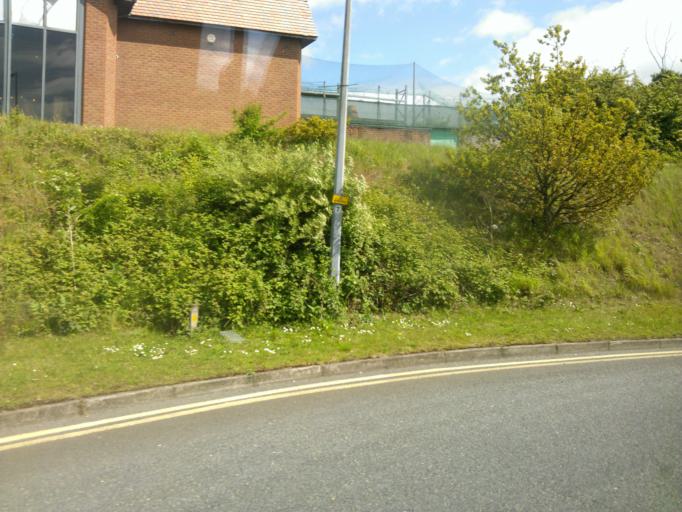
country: GB
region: England
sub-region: Essex
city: Eight Ash Green
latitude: 51.8854
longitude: 0.8350
